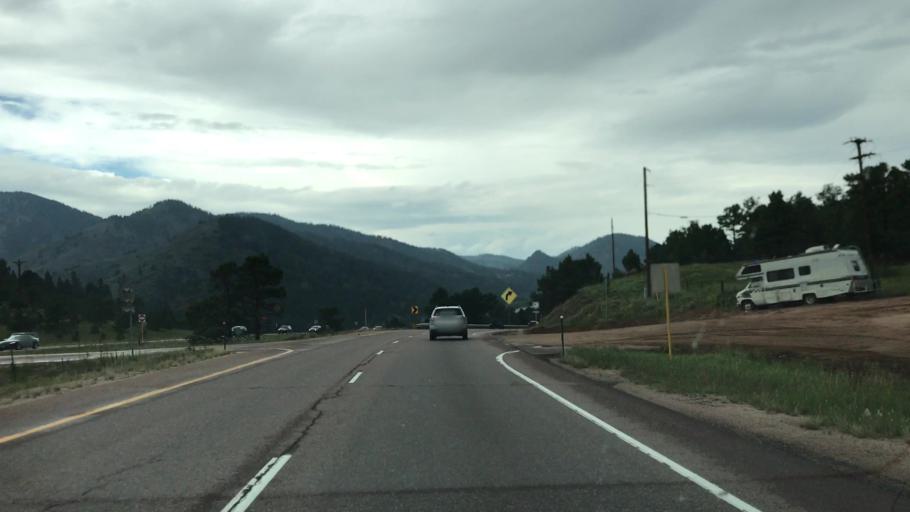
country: US
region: Colorado
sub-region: El Paso County
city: Cascade-Chipita Park
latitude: 38.9354
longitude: -105.0076
